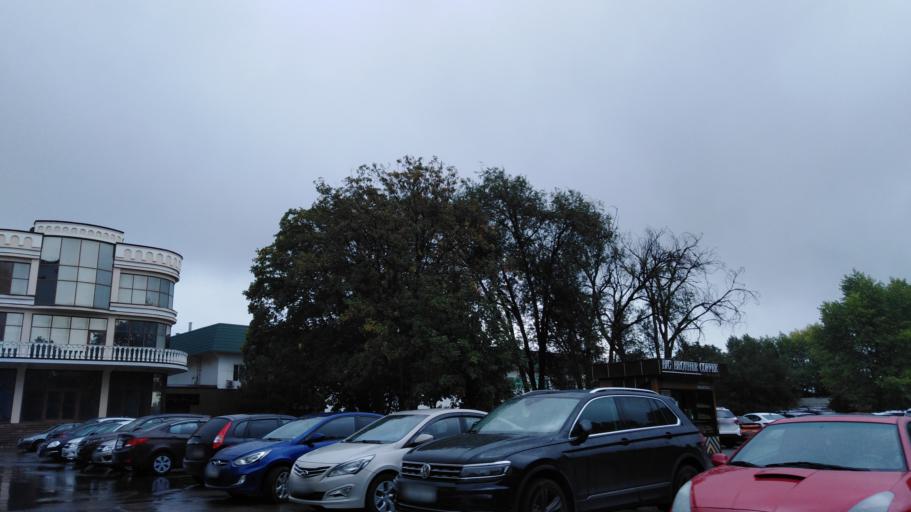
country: RU
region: Stavropol'skiy
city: Yessentukskaya
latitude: 44.0544
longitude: 42.9038
